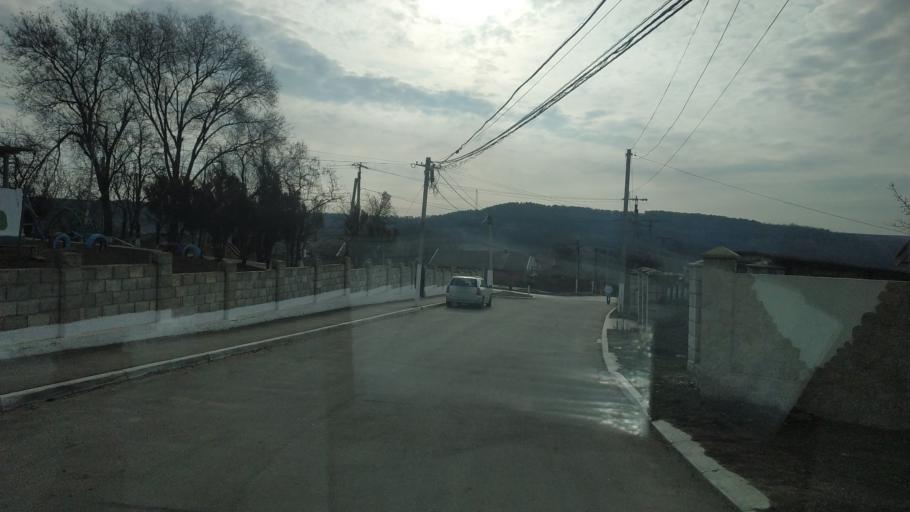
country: MD
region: Chisinau
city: Vadul lui Voda
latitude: 47.0097
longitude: 29.1217
